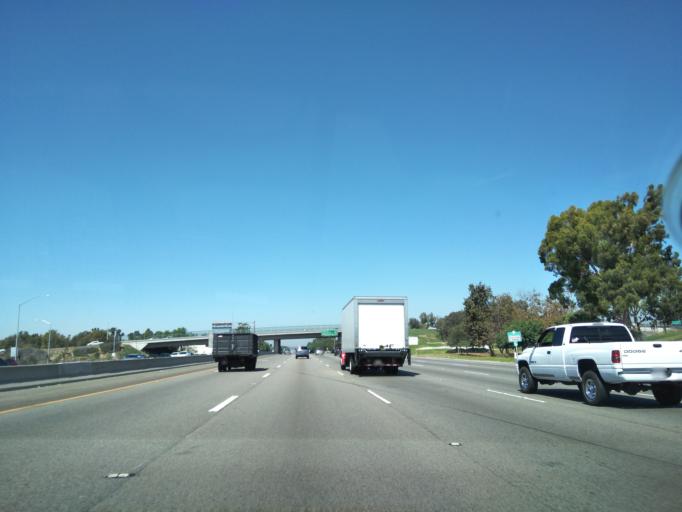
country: US
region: California
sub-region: Orange County
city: Irvine
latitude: 33.6882
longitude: -117.7671
